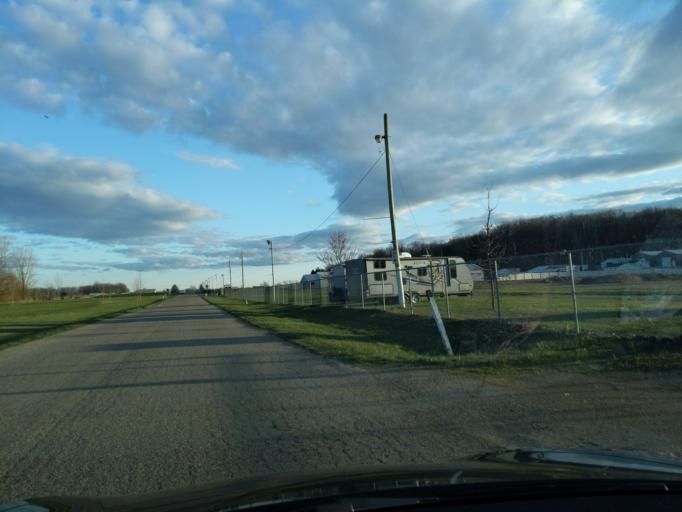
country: US
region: Michigan
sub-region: Ingham County
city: Mason
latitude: 42.5735
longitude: -84.4281
